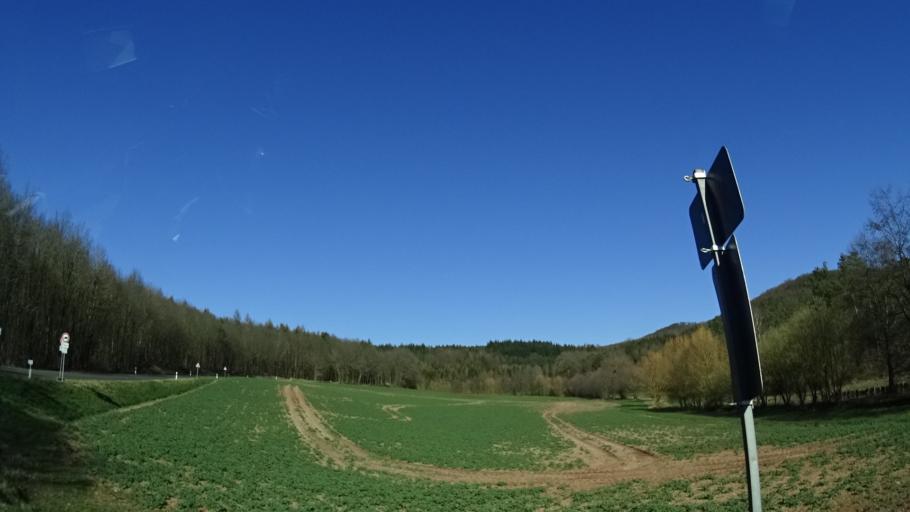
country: DE
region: Bavaria
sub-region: Regierungsbezirk Unterfranken
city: Willmars
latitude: 50.4785
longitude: 10.2576
